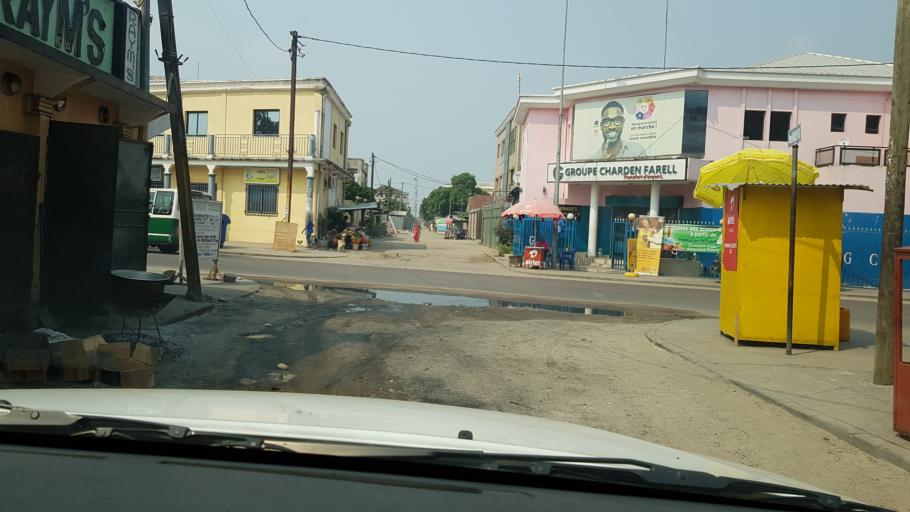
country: CG
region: Brazzaville
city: Brazzaville
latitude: -4.2588
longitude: 15.2603
